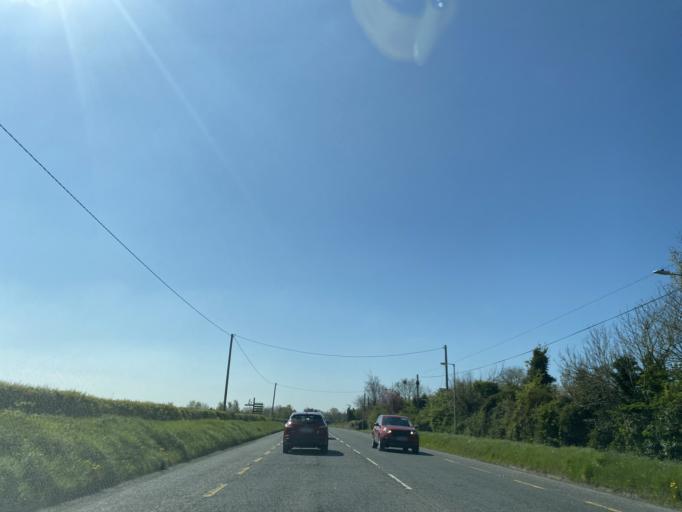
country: IE
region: Leinster
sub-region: Kildare
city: Maynooth
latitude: 53.3291
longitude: -6.6078
